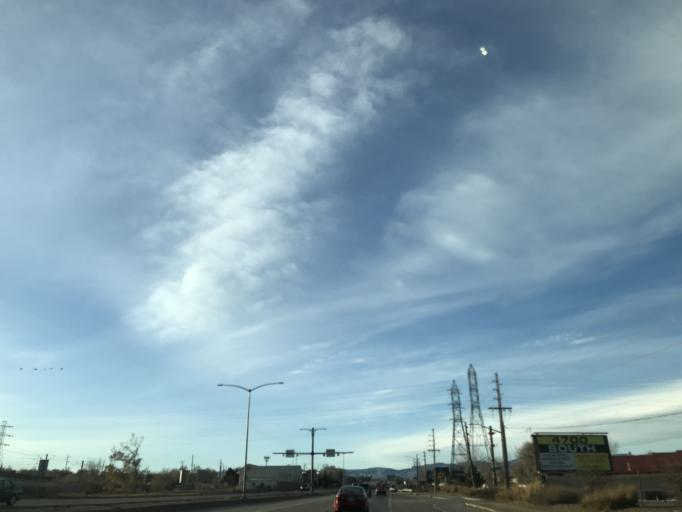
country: US
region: Colorado
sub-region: Arapahoe County
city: Littleton
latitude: 39.6306
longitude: -105.0094
